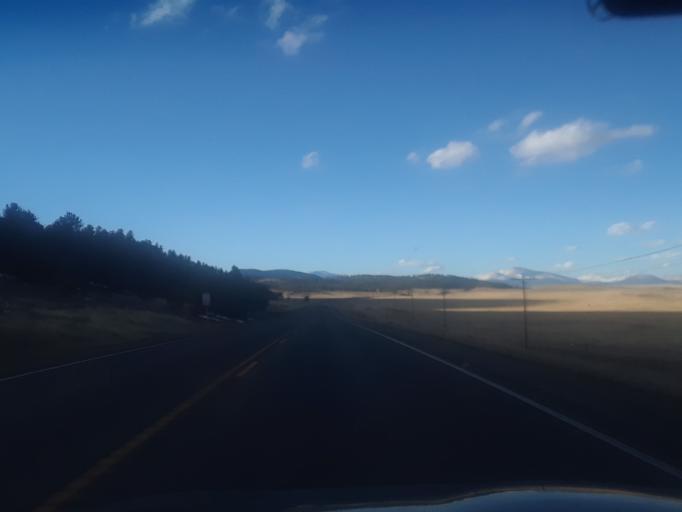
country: US
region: Colorado
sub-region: Park County
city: Fairplay
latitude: 39.0079
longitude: -105.9694
